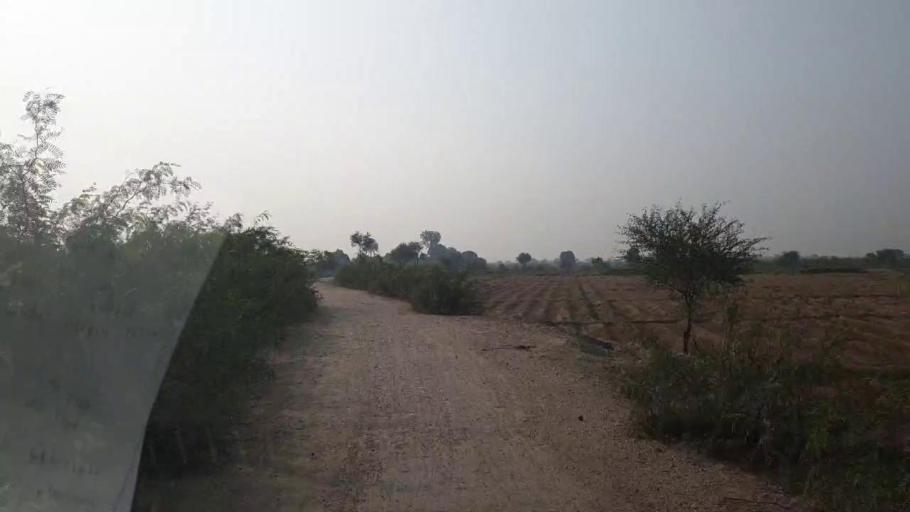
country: PK
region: Sindh
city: Tando Jam
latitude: 25.3313
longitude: 68.5261
